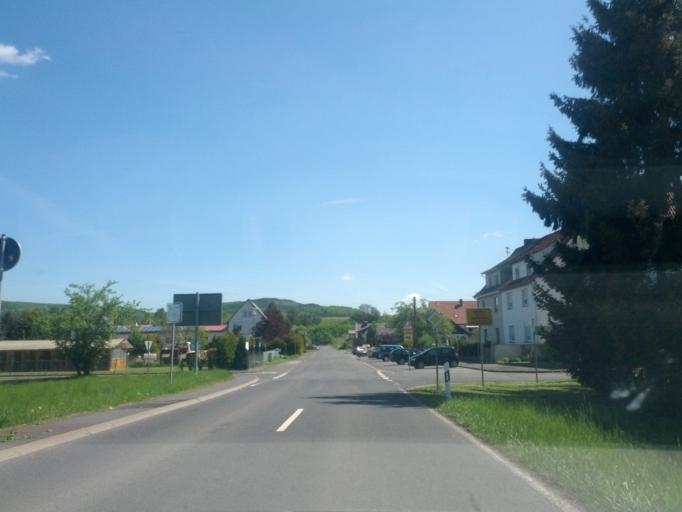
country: DE
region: Hesse
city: Wanfried
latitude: 51.1362
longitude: 10.1836
